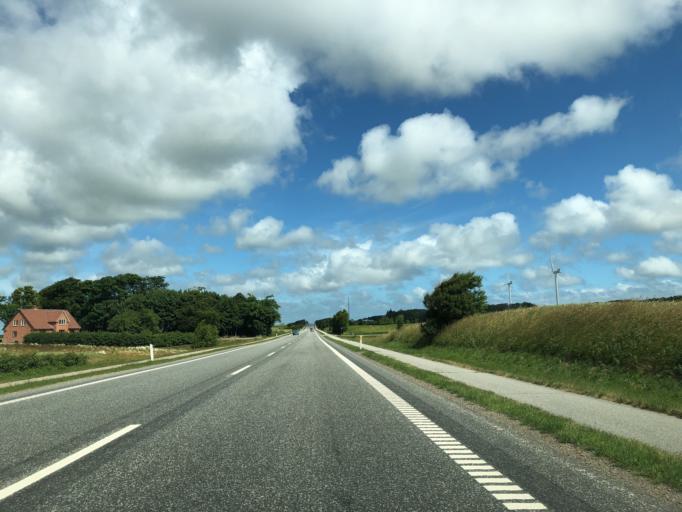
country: DK
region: Central Jutland
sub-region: Holstebro Kommune
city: Holstebro
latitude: 56.4106
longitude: 8.6043
